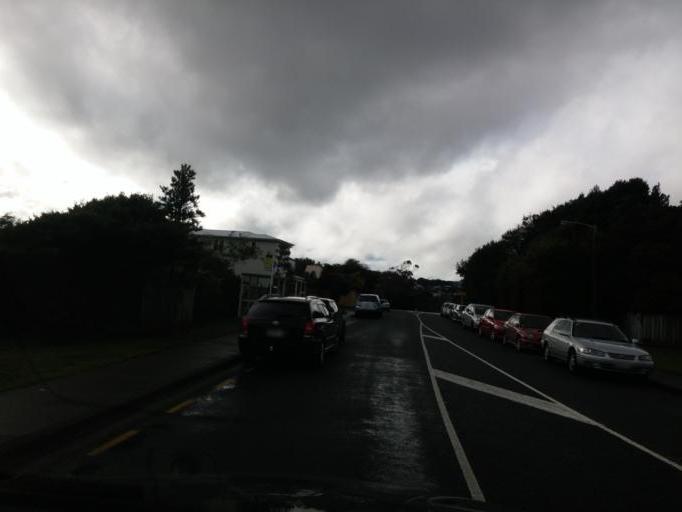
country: NZ
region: Wellington
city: Petone
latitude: -41.2071
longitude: 174.8048
